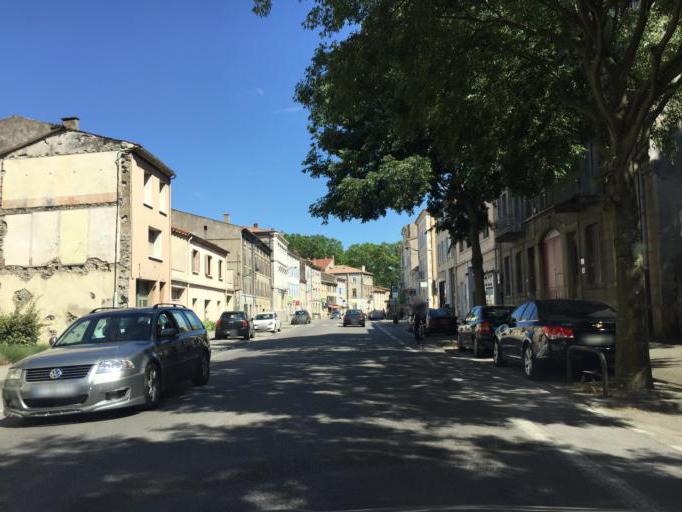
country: FR
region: Rhone-Alpes
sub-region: Departement de l'Ardeche
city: Tournon-sur-Rhone
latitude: 45.0711
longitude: 4.8258
